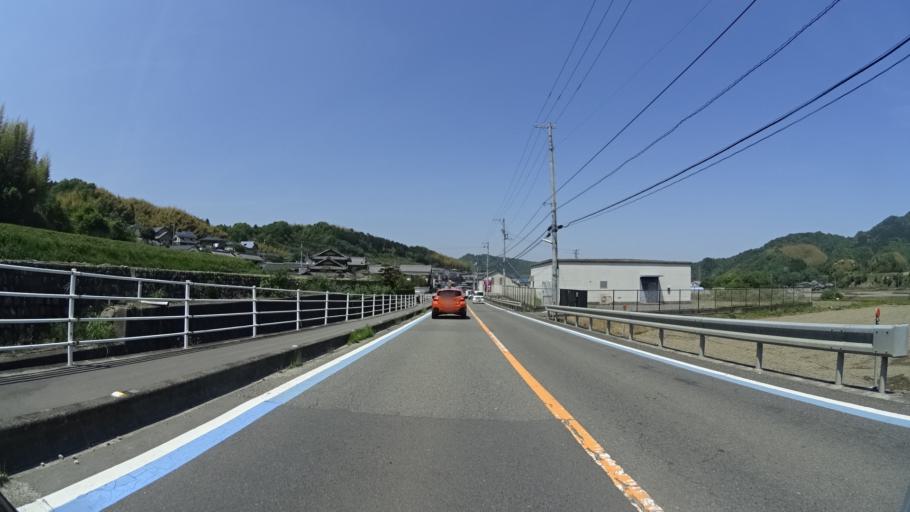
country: JP
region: Ehime
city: Hojo
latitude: 34.0101
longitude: 132.9376
